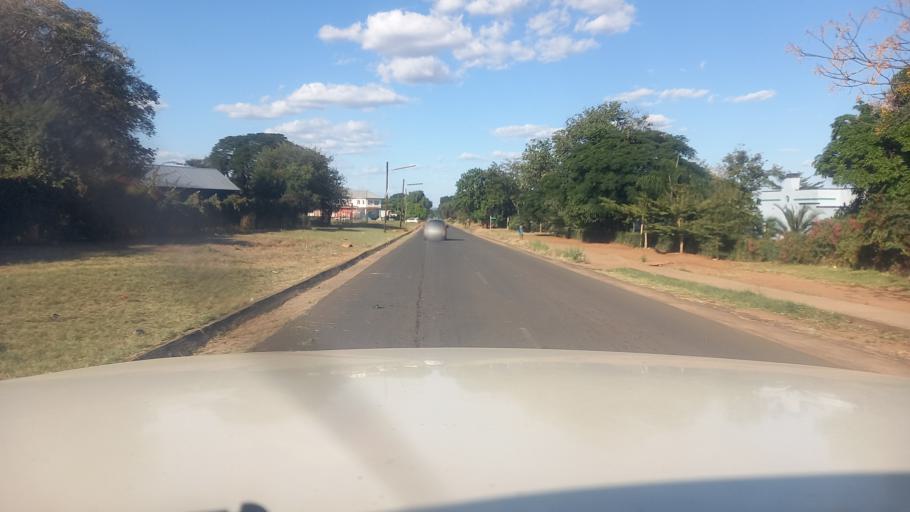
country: ZM
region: Southern
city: Livingstone
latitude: -17.8392
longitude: 25.8647
